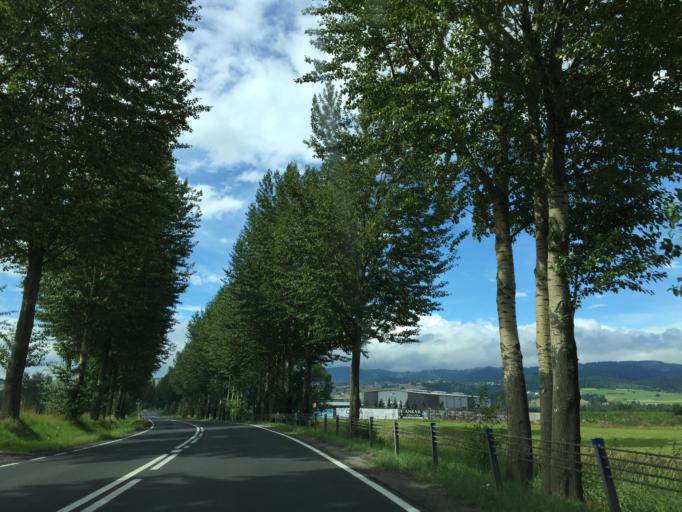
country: PL
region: Lesser Poland Voivodeship
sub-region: Powiat nowotarski
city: Waksmund
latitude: 49.4668
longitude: 20.0598
